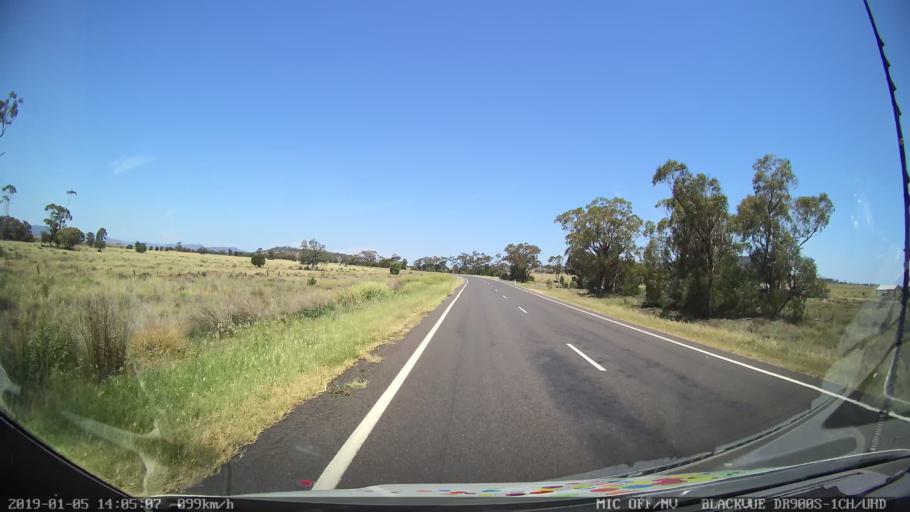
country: AU
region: New South Wales
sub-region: Gunnedah
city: Gunnedah
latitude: -31.2073
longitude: 150.3717
